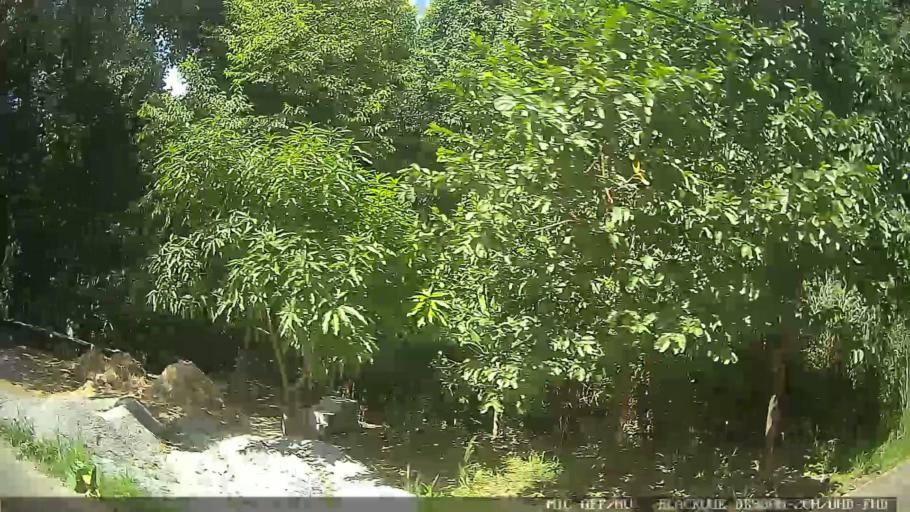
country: BR
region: Sao Paulo
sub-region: Atibaia
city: Atibaia
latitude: -23.1472
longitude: -46.5629
